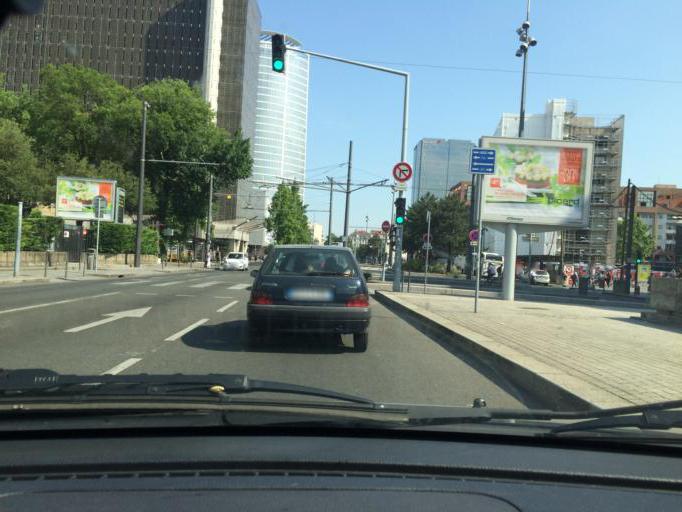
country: FR
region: Rhone-Alpes
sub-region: Departement du Rhone
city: Lyon
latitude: 45.7595
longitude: 4.8582
